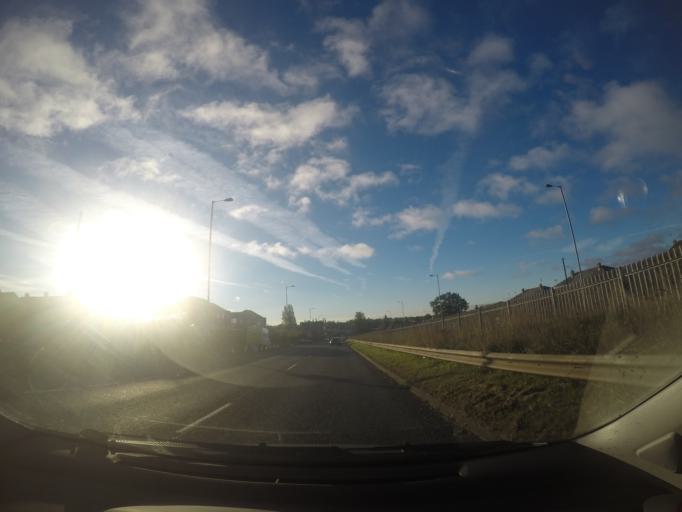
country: GB
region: England
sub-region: City and Borough of Leeds
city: Scholes
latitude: 53.8191
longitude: -1.4547
